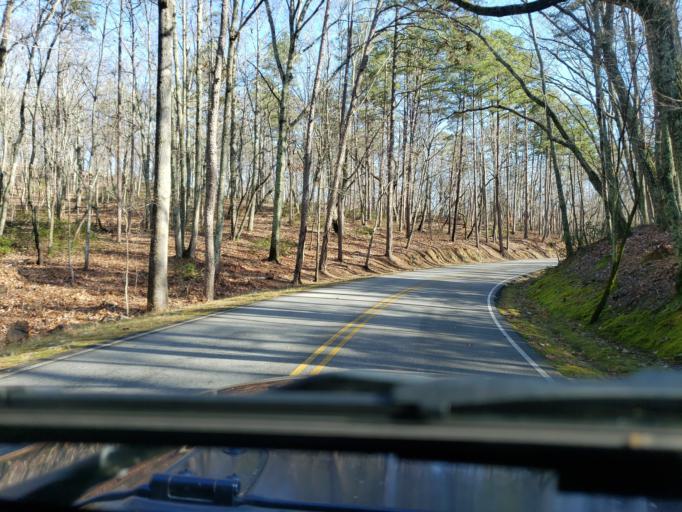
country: US
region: North Carolina
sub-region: Cleveland County
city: White Plains
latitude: 35.1501
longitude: -81.3911
